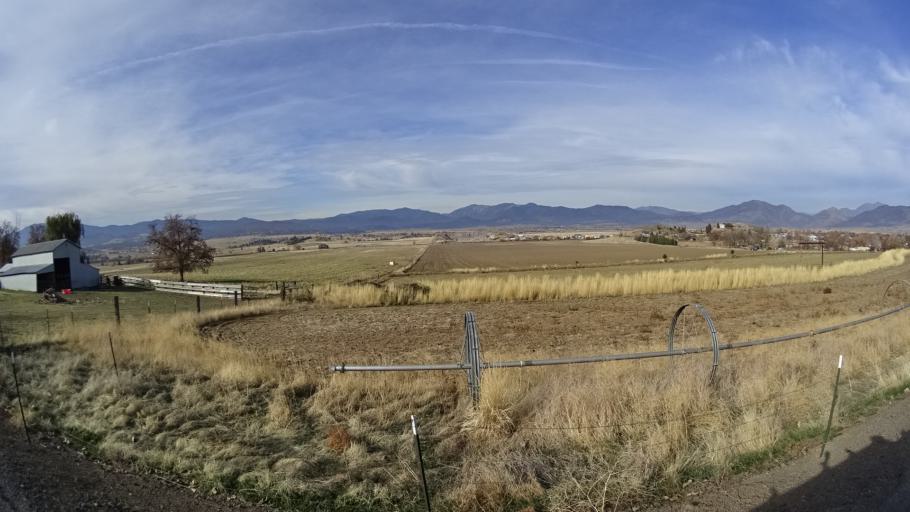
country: US
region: California
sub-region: Siskiyou County
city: Montague
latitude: 41.7166
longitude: -122.5214
